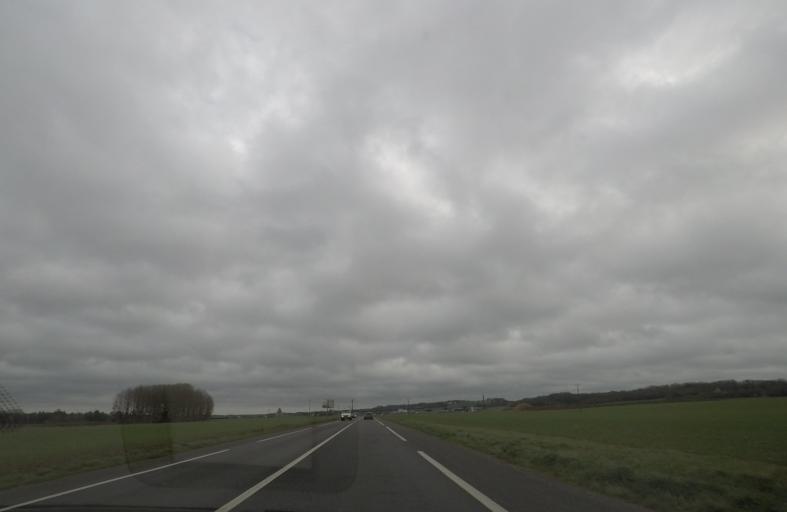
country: FR
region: Centre
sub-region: Departement du Loir-et-Cher
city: Villiers-sur-Loir
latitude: 47.7802
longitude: 1.0080
